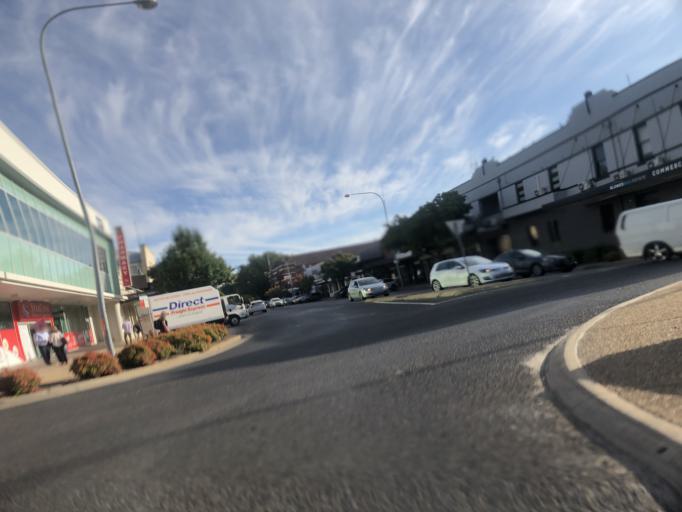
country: AU
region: New South Wales
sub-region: Orange Municipality
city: Orange
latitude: -33.2858
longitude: 149.1007
